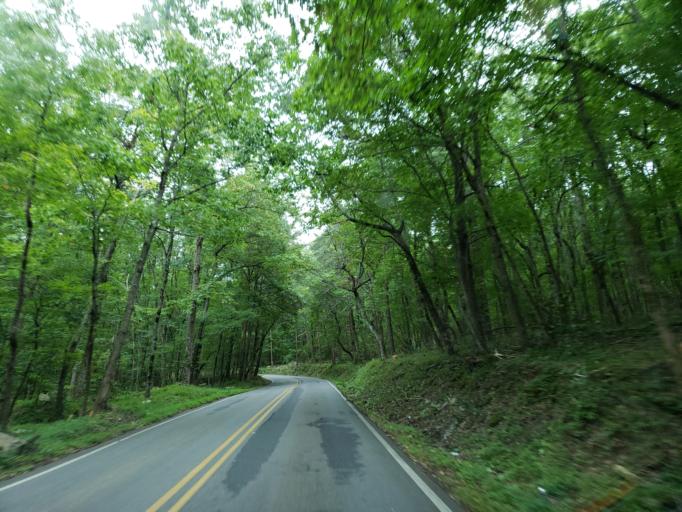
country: US
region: Georgia
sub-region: Pickens County
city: Jasper
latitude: 34.4111
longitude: -84.5289
